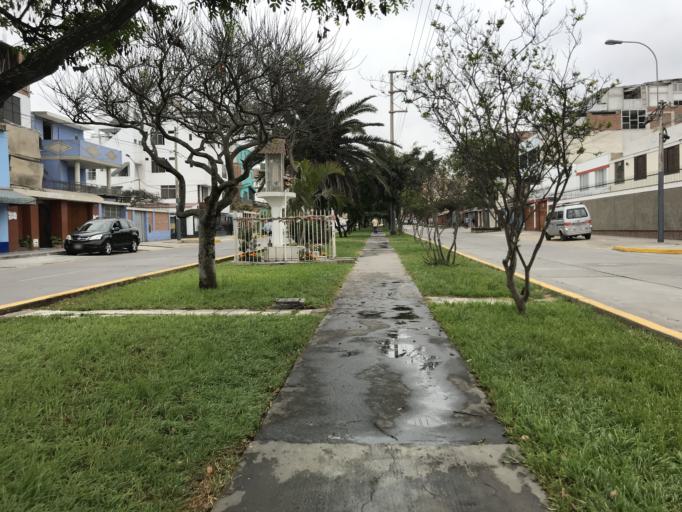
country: PE
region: Callao
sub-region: Callao
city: Callao
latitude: -12.0654
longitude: -77.0722
